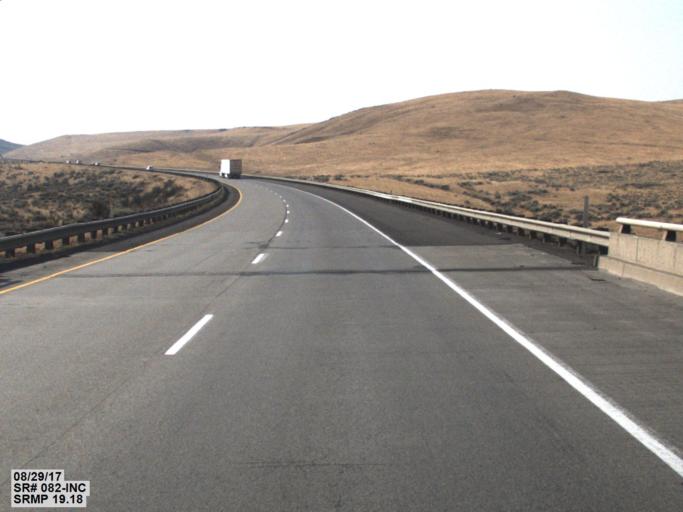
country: US
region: Washington
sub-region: Yakima County
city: Terrace Heights
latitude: 46.7473
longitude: -120.3905
